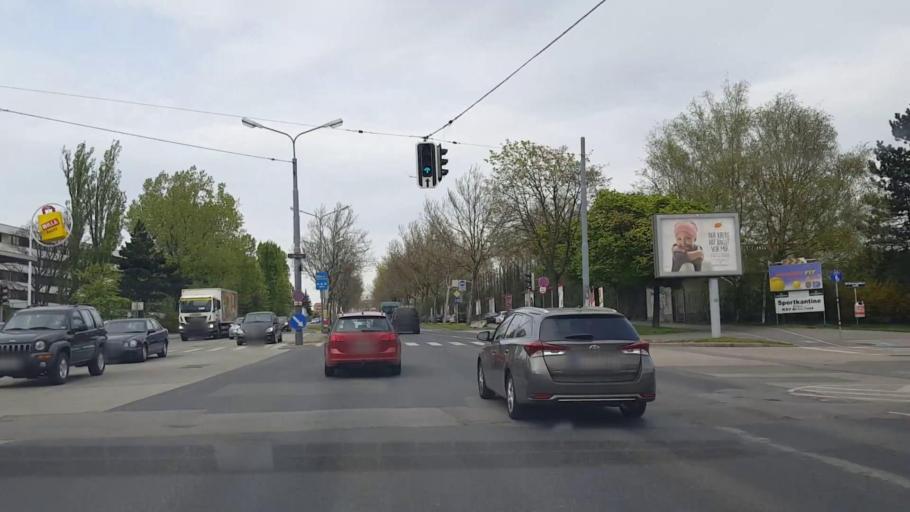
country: AT
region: Lower Austria
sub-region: Politischer Bezirk Modling
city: Vosendorf
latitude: 48.1589
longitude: 16.3667
